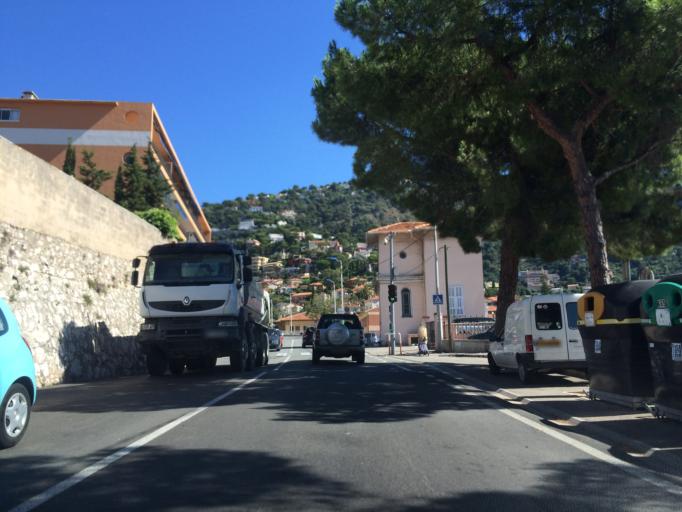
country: FR
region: Provence-Alpes-Cote d'Azur
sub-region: Departement des Alpes-Maritimes
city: Villefranche-sur-Mer
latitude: 43.7038
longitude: 7.3093
